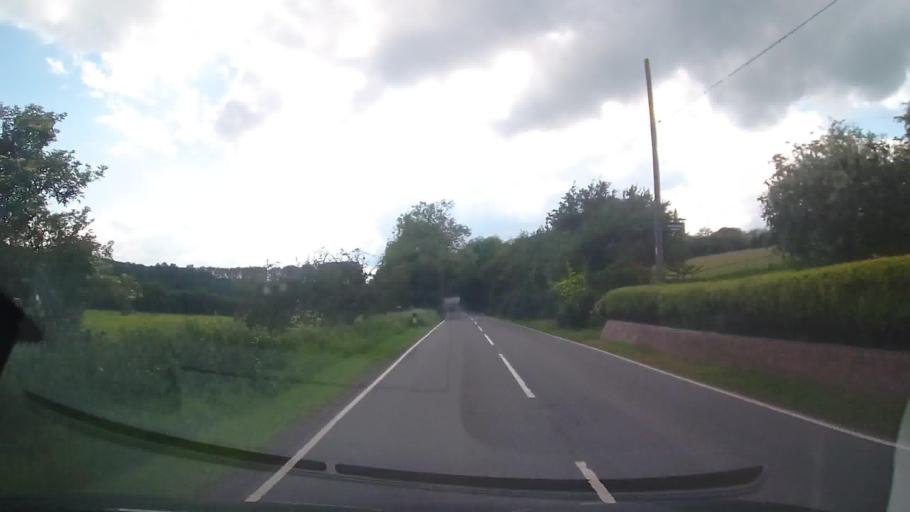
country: GB
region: England
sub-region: Shropshire
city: Much Wenlock
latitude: 52.6410
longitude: -2.5502
